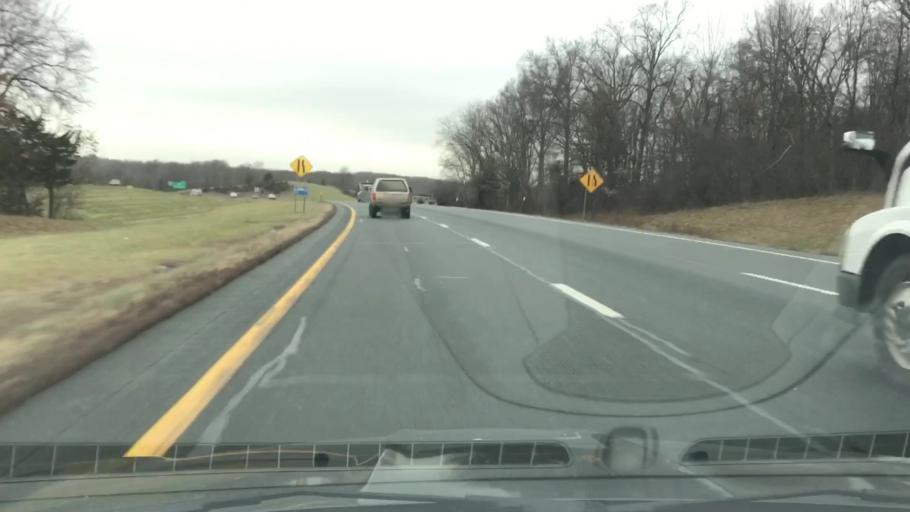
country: US
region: New York
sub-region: Orange County
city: Orange Lake
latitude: 41.5221
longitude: -74.0970
